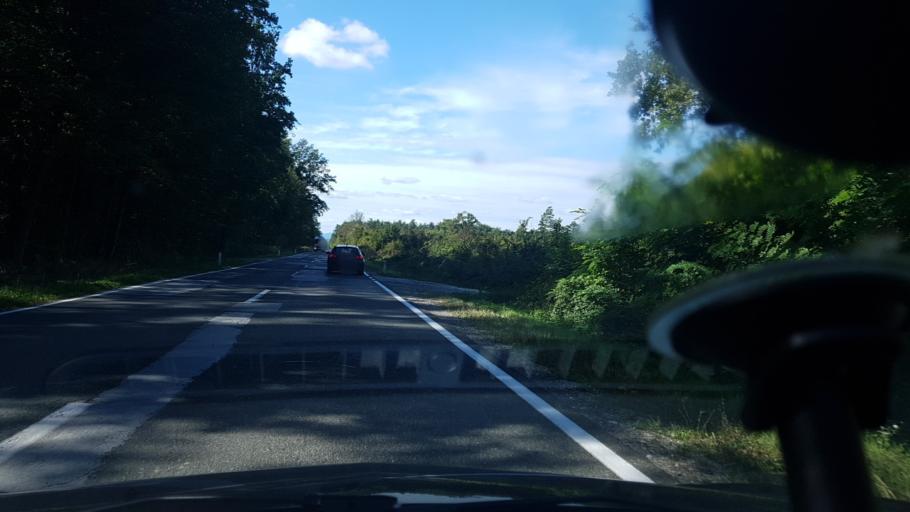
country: SI
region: Kidricevo
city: Kidricevo
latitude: 46.4106
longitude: 15.7724
